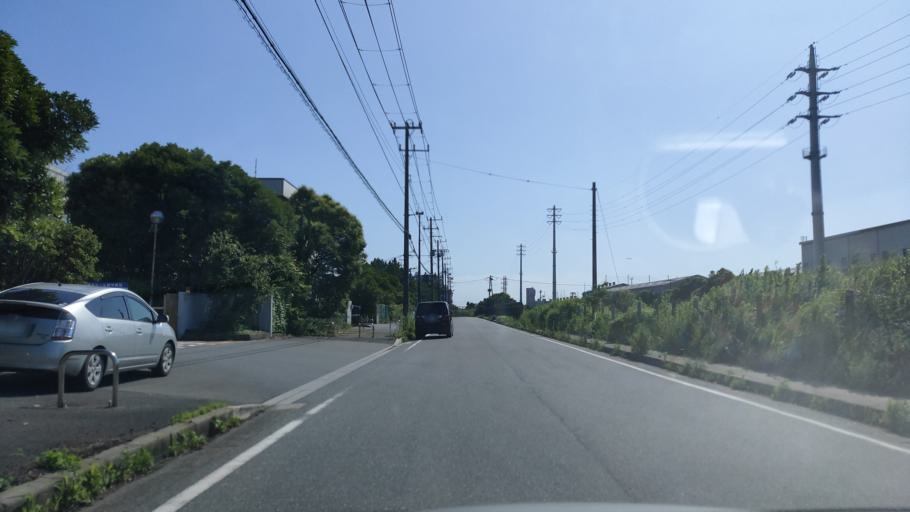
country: JP
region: Tokyo
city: Urayasu
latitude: 35.6334
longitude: 139.9024
